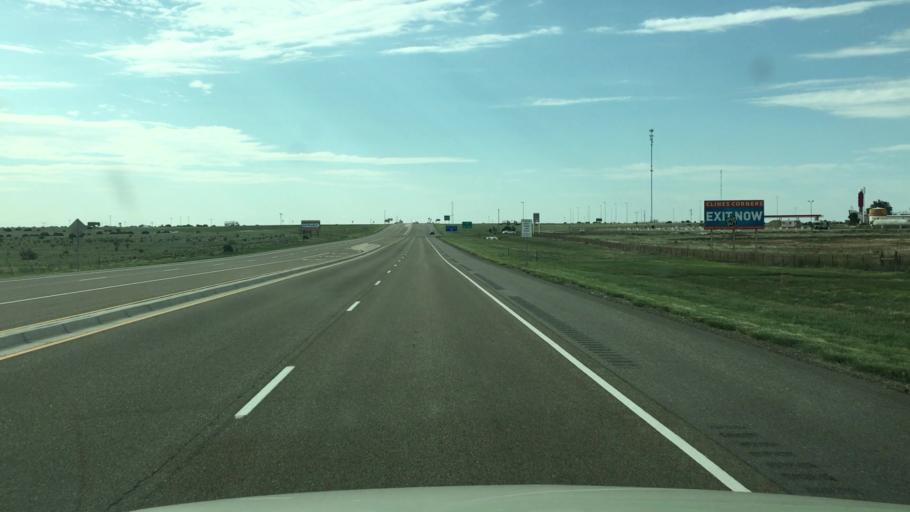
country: US
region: New Mexico
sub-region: Torrance County
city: Moriarty
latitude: 35.0149
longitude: -105.6680
